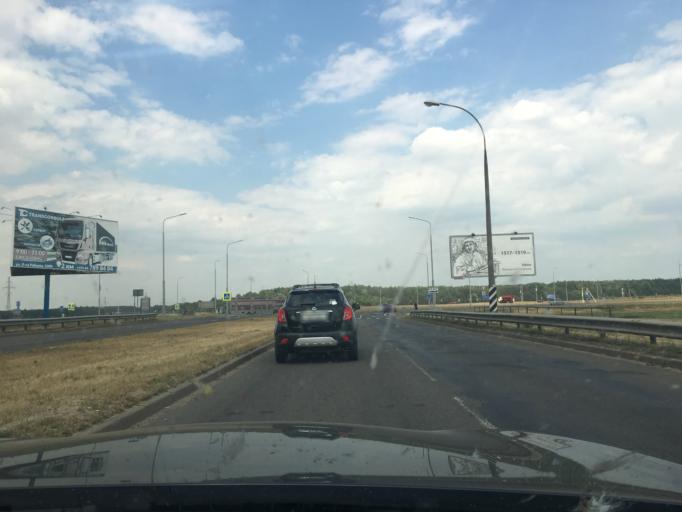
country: BY
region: Brest
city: Brest
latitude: 52.1506
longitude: 23.6897
